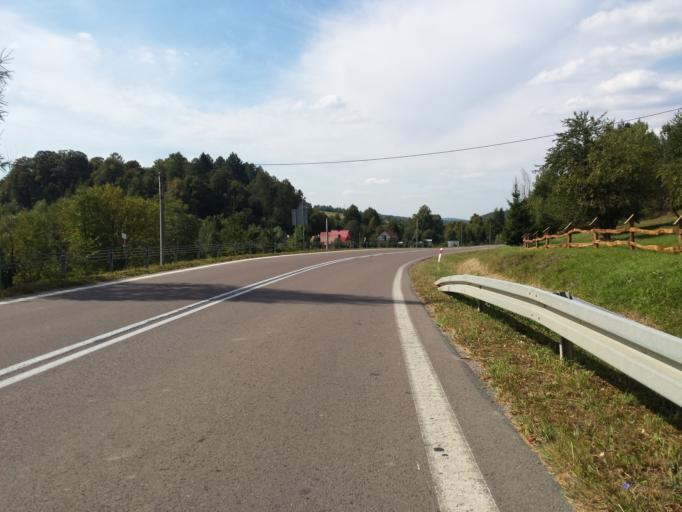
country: PL
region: Subcarpathian Voivodeship
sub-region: Powiat bieszczadzki
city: Ustrzyki Dolne
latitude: 49.5429
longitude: 22.5873
